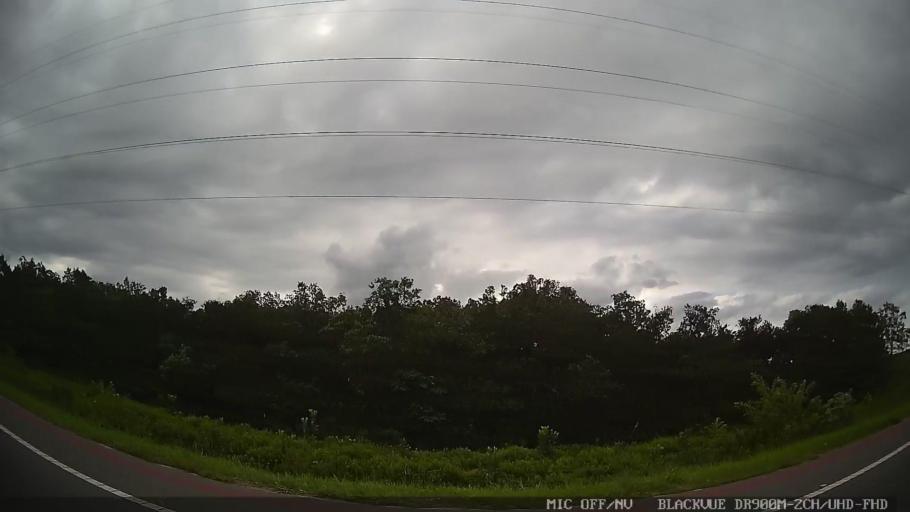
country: BR
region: Sao Paulo
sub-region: Itanhaem
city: Itanhaem
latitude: -24.1800
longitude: -46.8075
